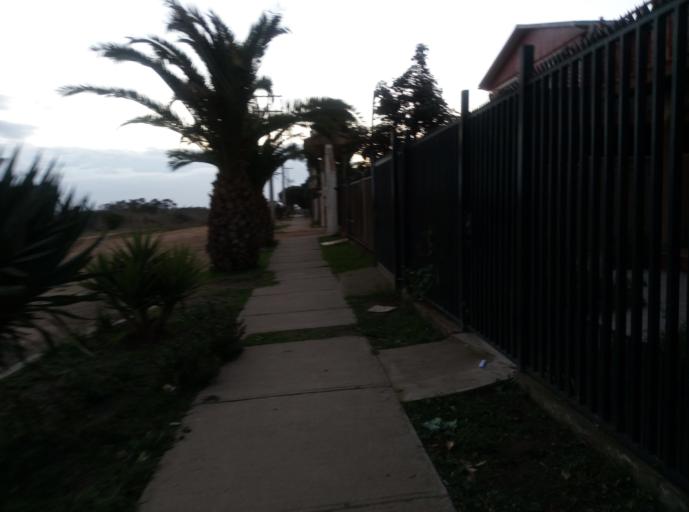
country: CL
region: Valparaiso
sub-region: San Antonio Province
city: El Tabo
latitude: -33.4226
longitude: -71.6905
